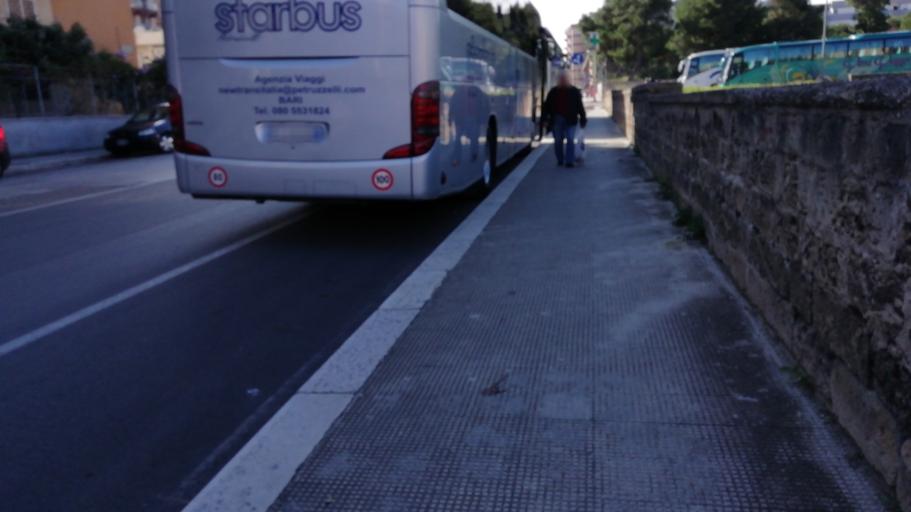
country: IT
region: Apulia
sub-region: Provincia di Bari
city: Bari
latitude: 41.1102
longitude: 16.8948
